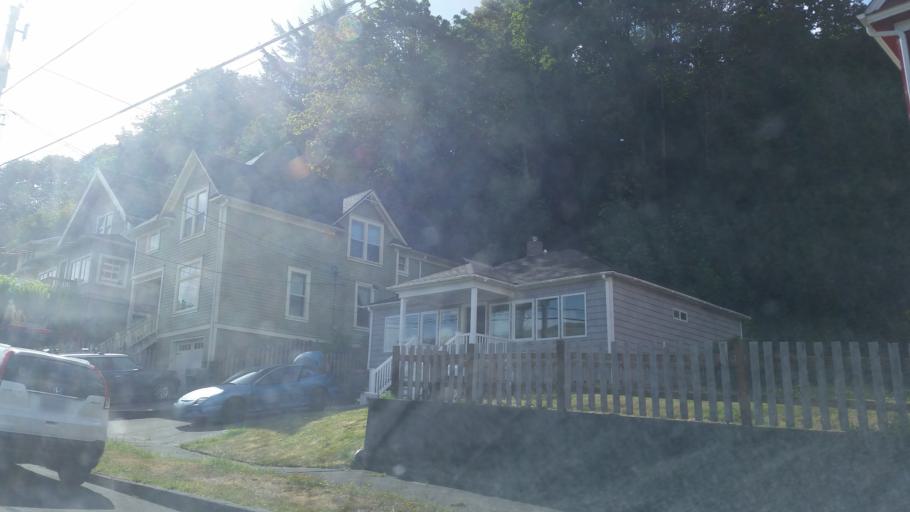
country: US
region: Oregon
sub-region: Clatsop County
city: Astoria
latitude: 46.1914
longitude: -123.8042
